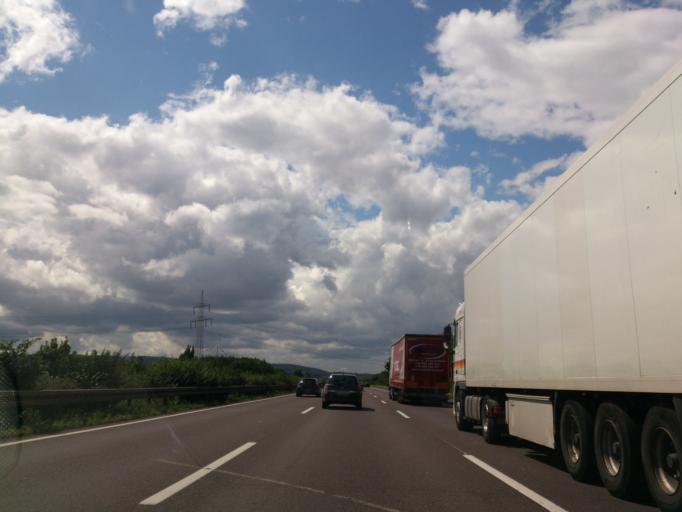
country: DE
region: Lower Saxony
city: Gross Munzel
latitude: 52.3638
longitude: 9.4387
